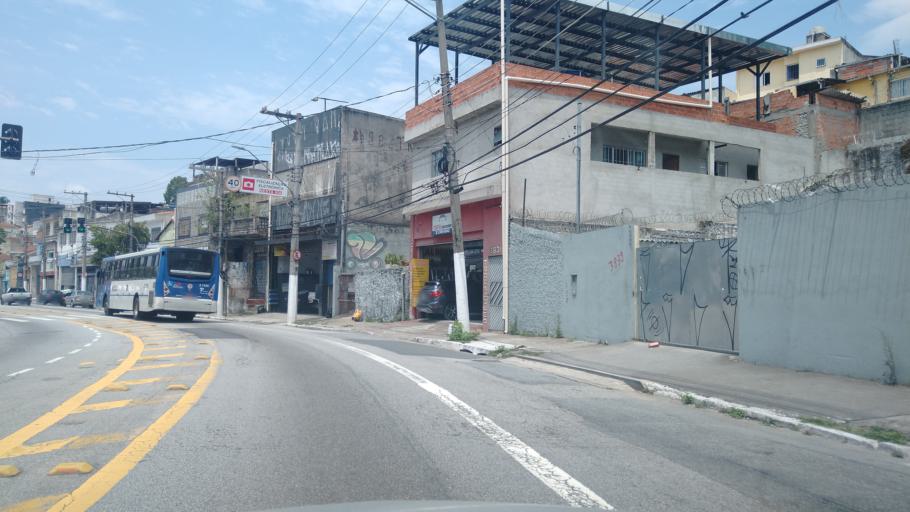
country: BR
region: Sao Paulo
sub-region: Sao Paulo
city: Sao Paulo
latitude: -23.4785
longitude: -46.6626
